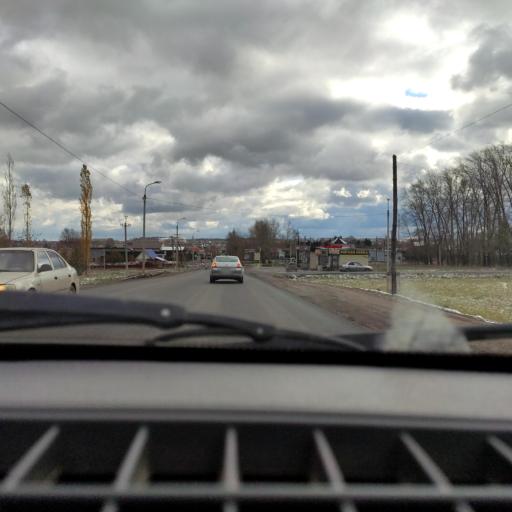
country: RU
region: Bashkortostan
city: Kabakovo
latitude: 54.6272
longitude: 56.1028
